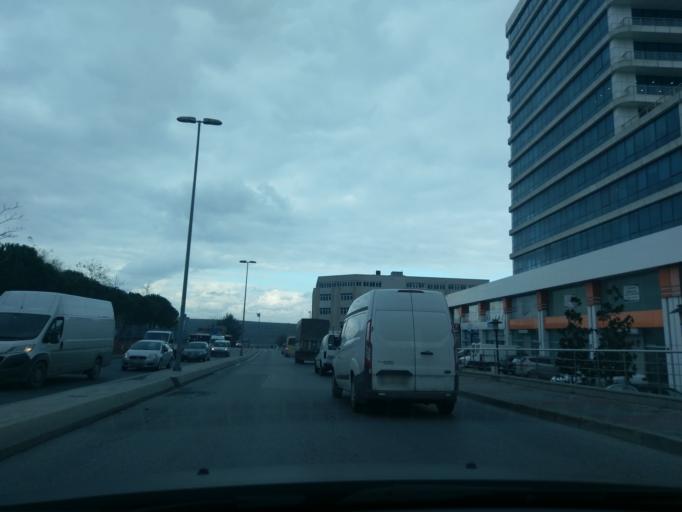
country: TR
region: Istanbul
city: Basaksehir
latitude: 41.0802
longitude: 28.8055
